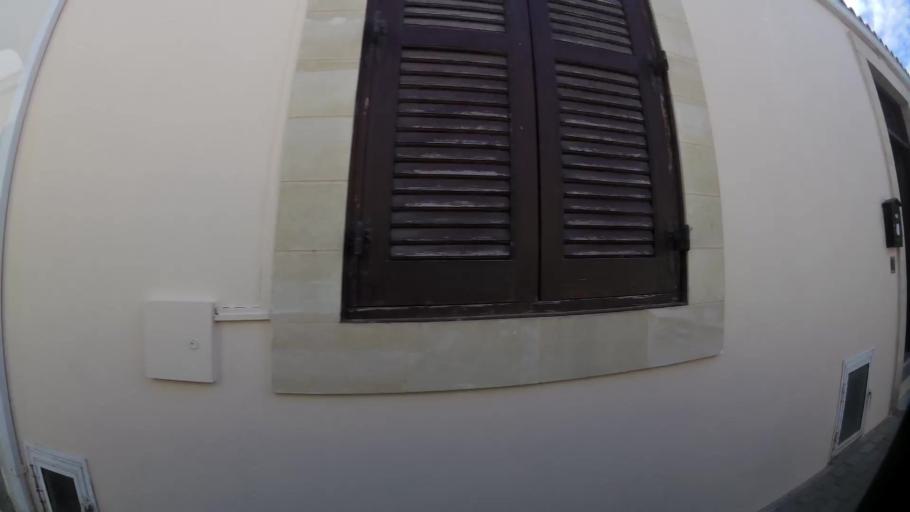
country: CY
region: Lefkosia
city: Nicosia
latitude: 35.1868
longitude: 33.3794
